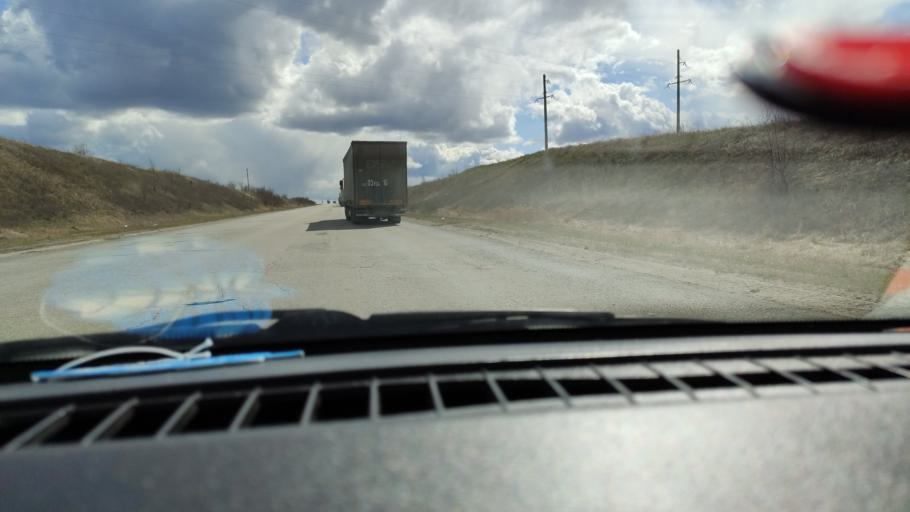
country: RU
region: Samara
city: Varlamovo
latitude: 53.0914
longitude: 48.3555
